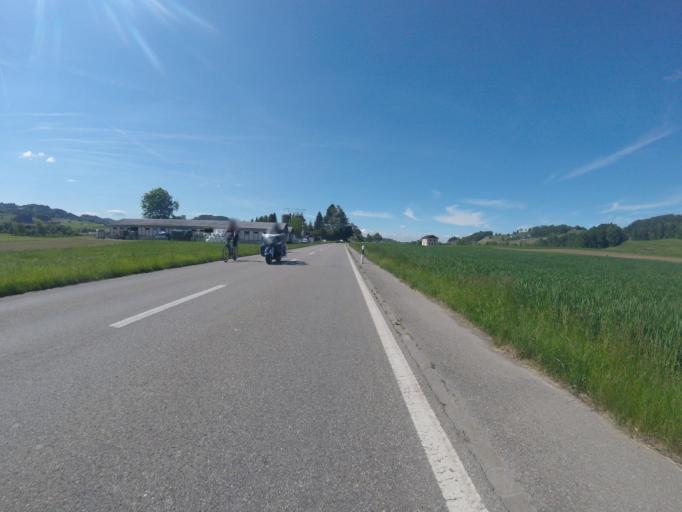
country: CH
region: Saint Gallen
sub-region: Wahlkreis Toggenburg
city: Ganterschwil
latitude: 47.3846
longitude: 9.0862
